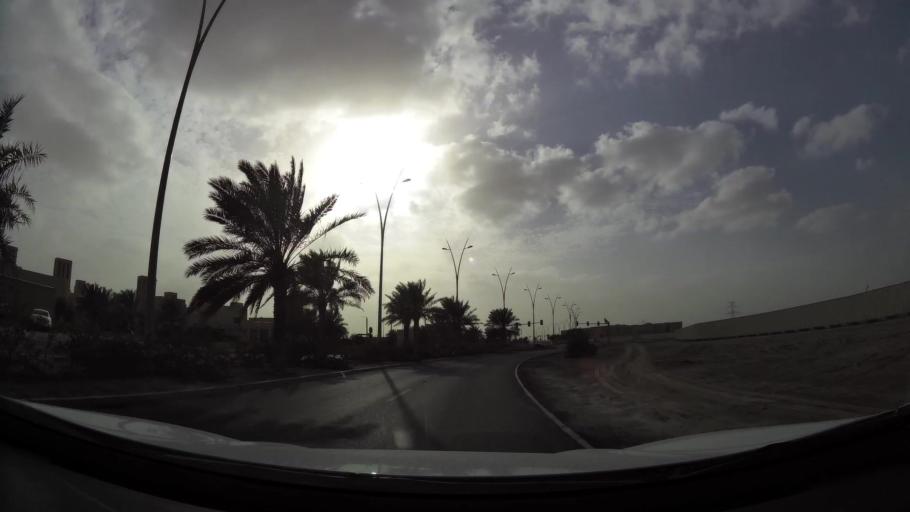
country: AE
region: Abu Dhabi
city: Abu Dhabi
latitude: 24.5041
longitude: 54.5970
